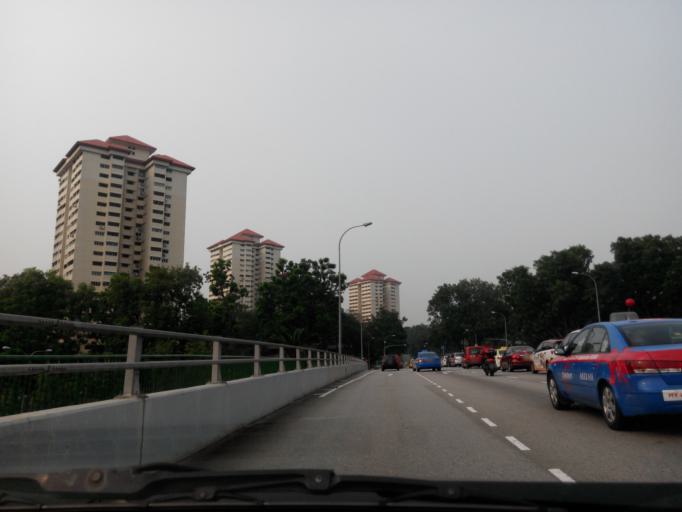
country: SG
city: Singapore
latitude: 1.2895
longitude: 103.7935
